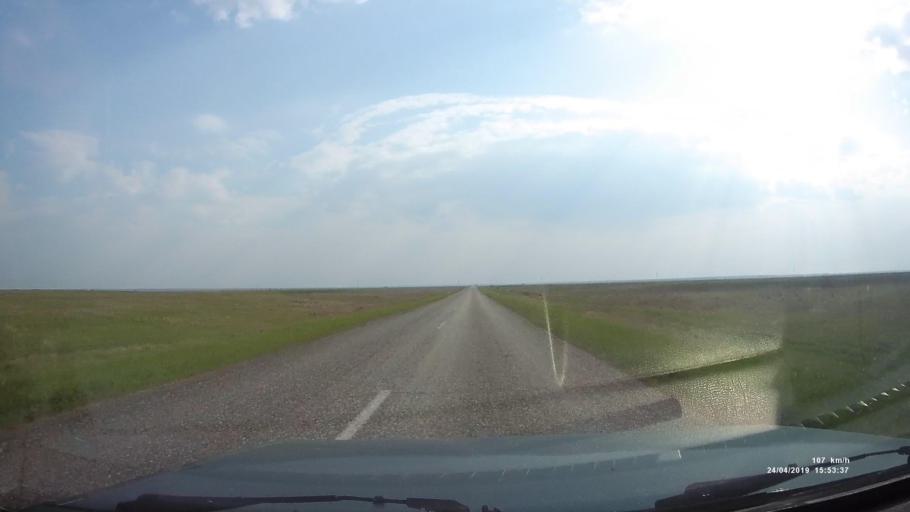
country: RU
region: Kalmykiya
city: Yashalta
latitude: 46.5959
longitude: 42.5733
